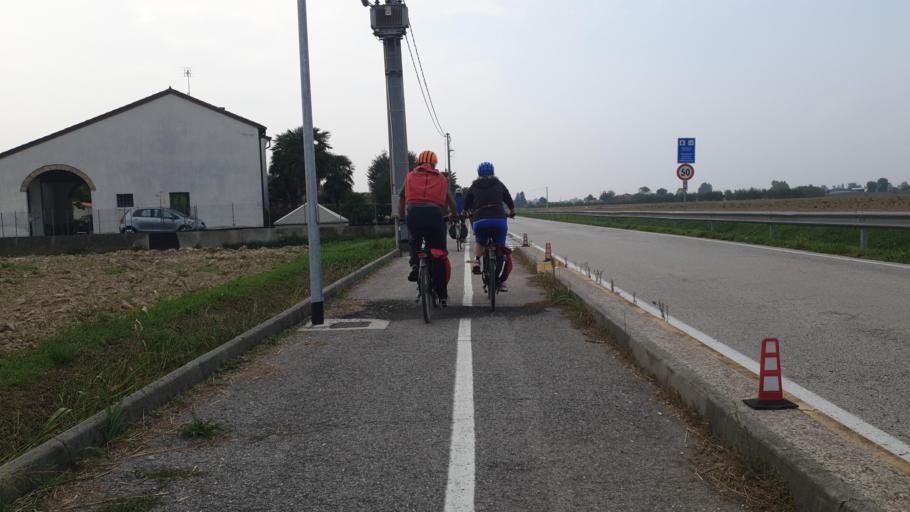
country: IT
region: Veneto
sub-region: Provincia di Padova
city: Brugine
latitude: 45.3087
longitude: 11.9927
